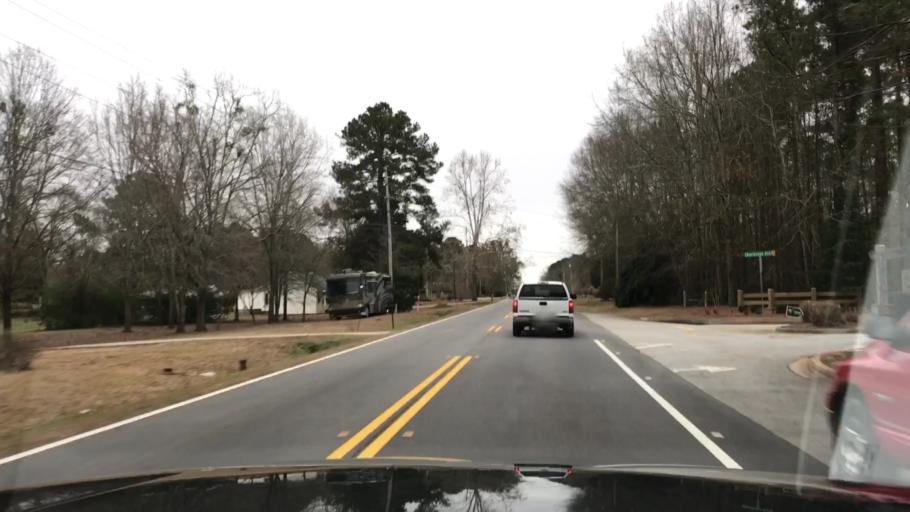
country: US
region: Georgia
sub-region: Walton County
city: Monroe
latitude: 33.8544
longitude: -83.7367
